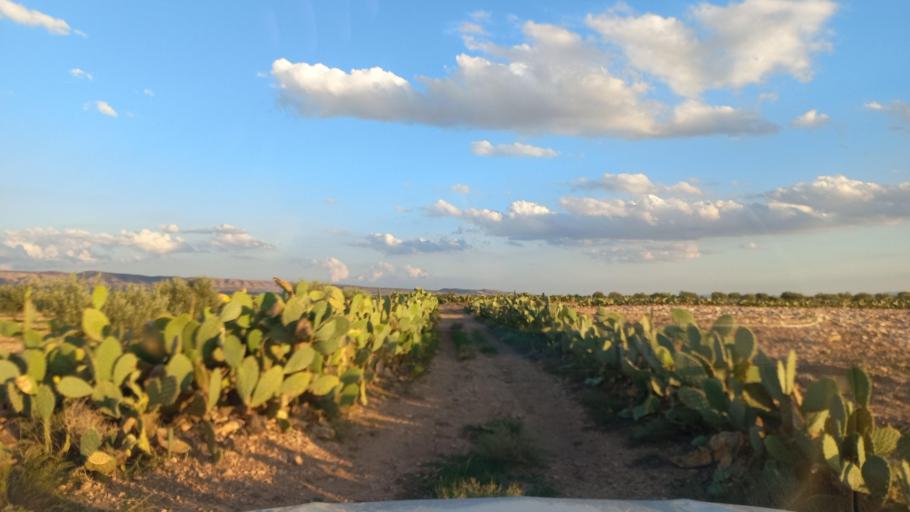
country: TN
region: Al Qasrayn
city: Sbiba
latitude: 35.3741
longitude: 9.0533
